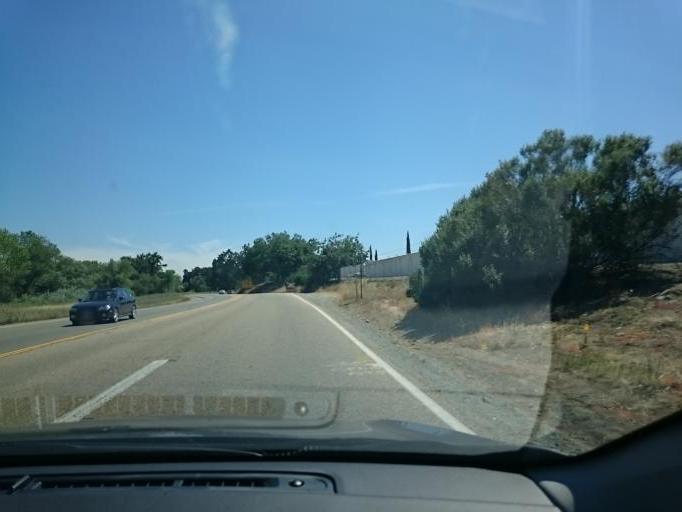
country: US
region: California
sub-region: Calaveras County
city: Valley Springs
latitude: 38.1778
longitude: -120.8310
